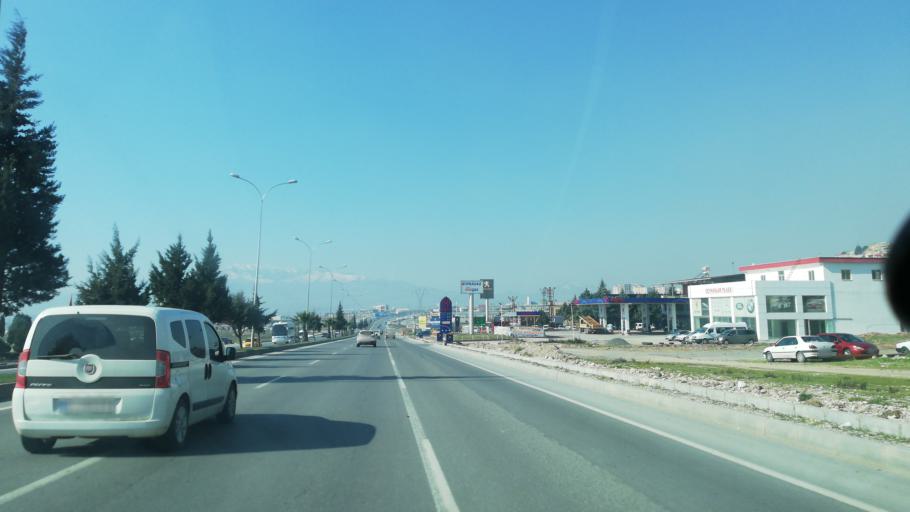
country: TR
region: Kahramanmaras
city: Kahramanmaras
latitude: 37.5656
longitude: 36.9012
